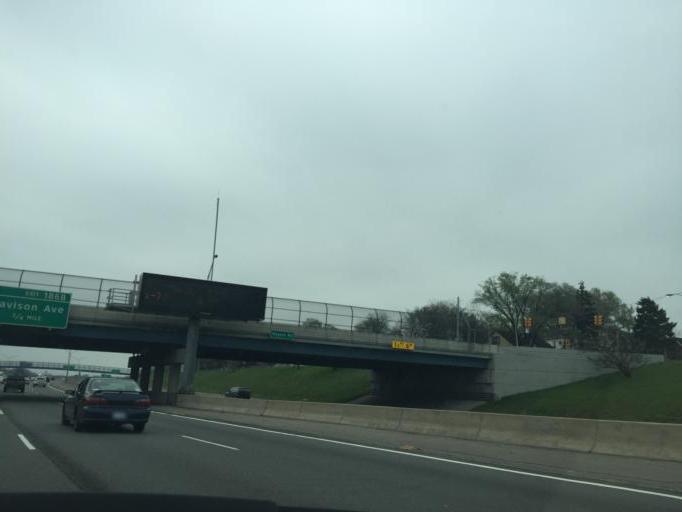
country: US
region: Michigan
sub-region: Wayne County
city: Dearborn
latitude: 42.3851
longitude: -83.1693
